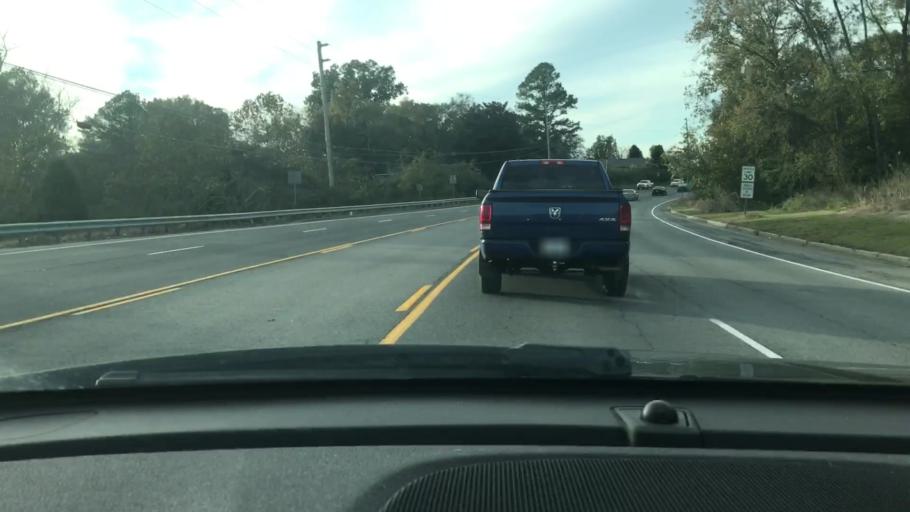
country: US
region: Tennessee
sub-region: Cheatham County
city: Ashland City
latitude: 36.2628
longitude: -87.0568
